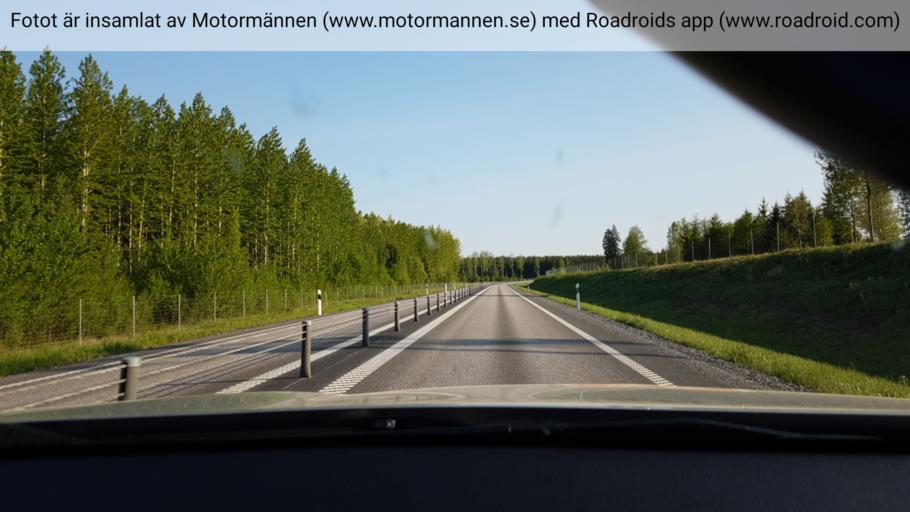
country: SE
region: Uppsala
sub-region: Heby Kommun
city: Heby
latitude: 59.9853
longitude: 16.8533
